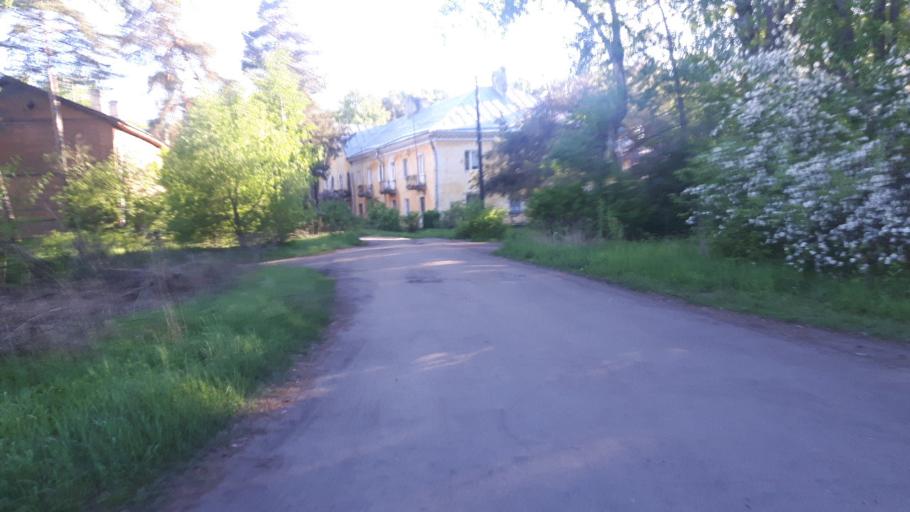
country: RU
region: St.-Petersburg
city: Bol'shaya Izhora
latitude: 59.9464
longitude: 29.5692
